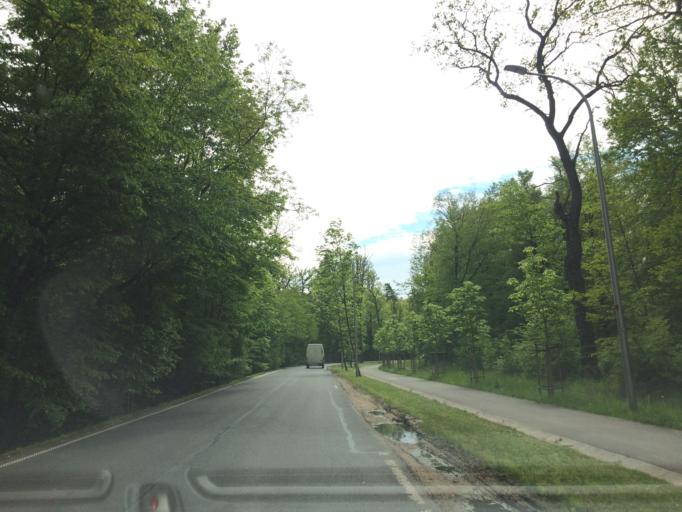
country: PL
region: Lower Silesian Voivodeship
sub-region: Powiat wroclawski
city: Smolec
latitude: 51.1529
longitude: 16.8728
